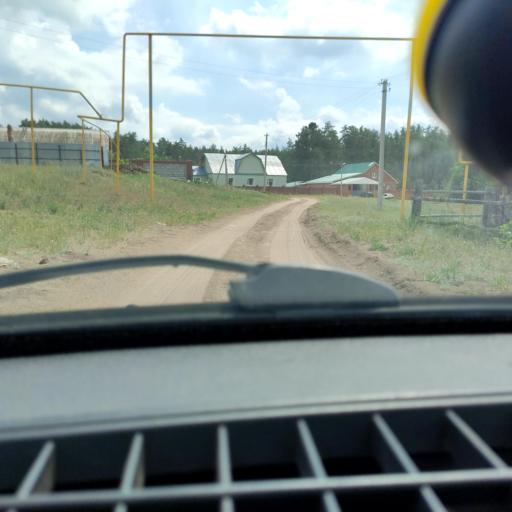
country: RU
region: Samara
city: Povolzhskiy
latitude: 53.6341
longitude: 49.6811
